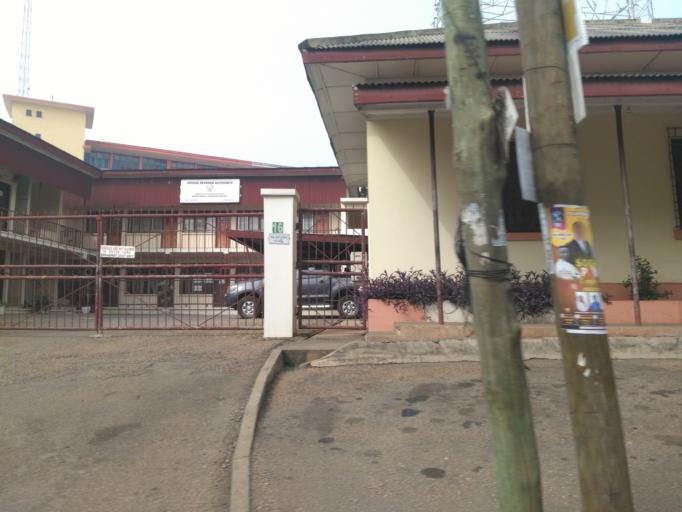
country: GH
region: Ashanti
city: Kumasi
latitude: 6.6915
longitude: -1.6231
